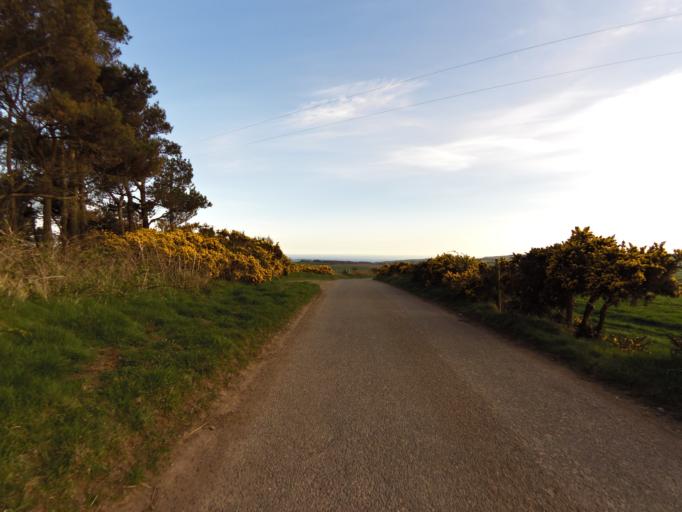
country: GB
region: Scotland
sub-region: Aberdeenshire
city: Stonehaven
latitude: 56.9205
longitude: -2.2277
